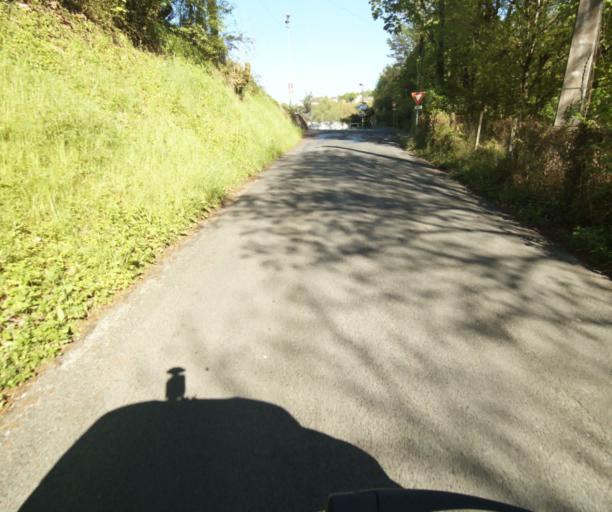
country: FR
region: Limousin
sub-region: Departement de la Correze
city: Tulle
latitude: 45.2747
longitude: 1.7774
